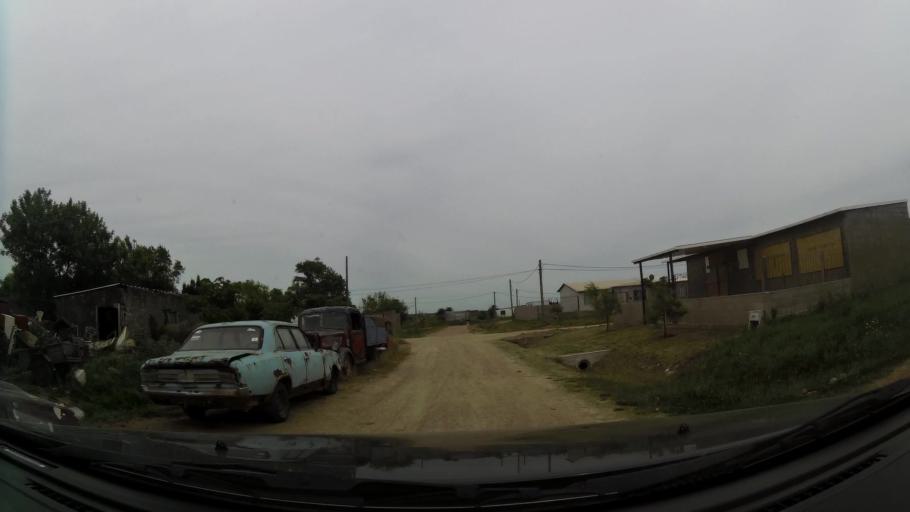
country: UY
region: Canelones
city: La Paz
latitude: -34.7474
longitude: -56.2337
